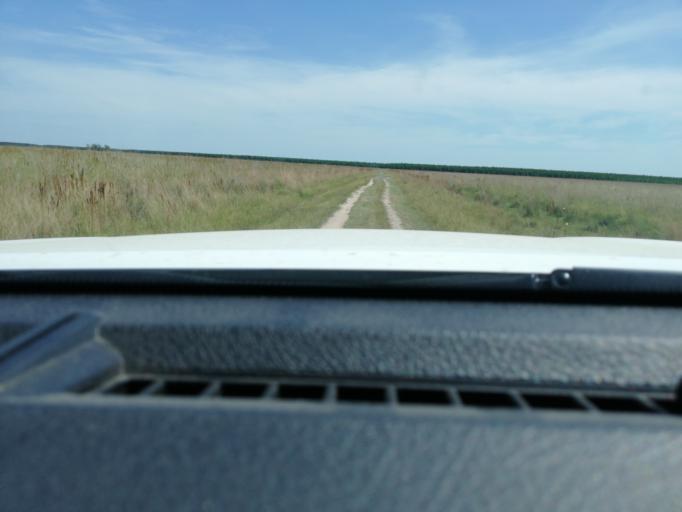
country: AR
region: Corrientes
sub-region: Departamento de San Miguel
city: San Miguel
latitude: -28.0501
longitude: -57.4556
